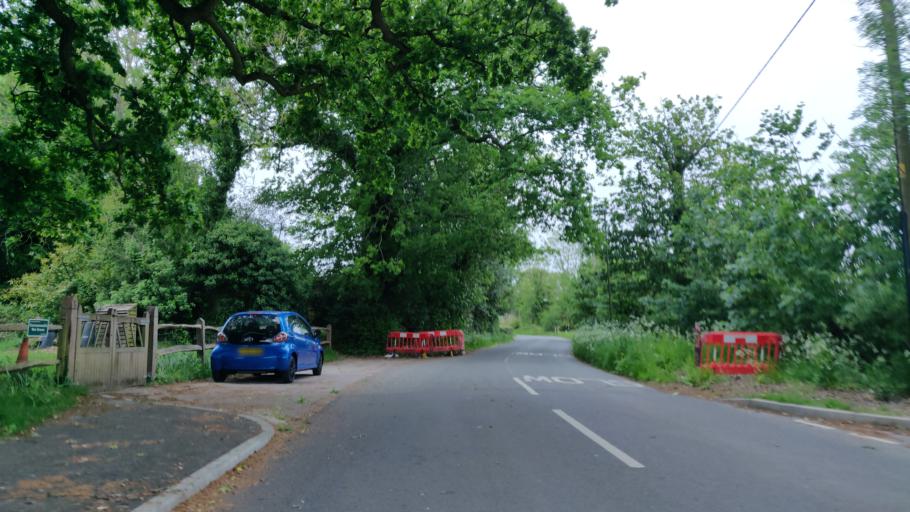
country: GB
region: England
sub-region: West Sussex
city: Southwater
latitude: 51.0247
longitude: -0.3571
